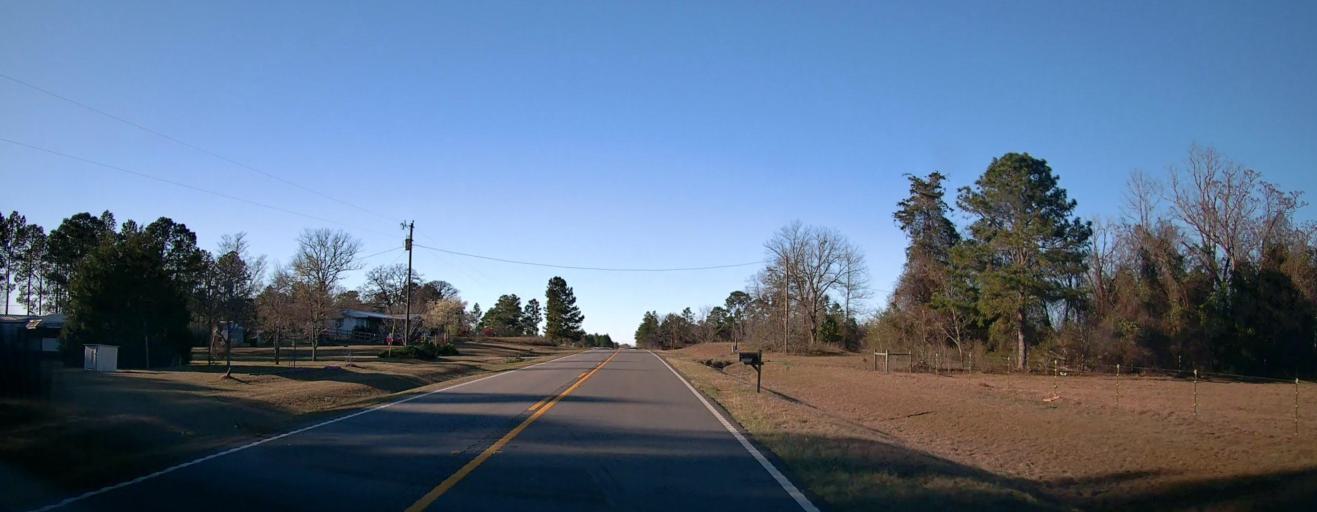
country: US
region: Georgia
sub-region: Talbot County
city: Talbotton
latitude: 32.5240
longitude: -84.4295
